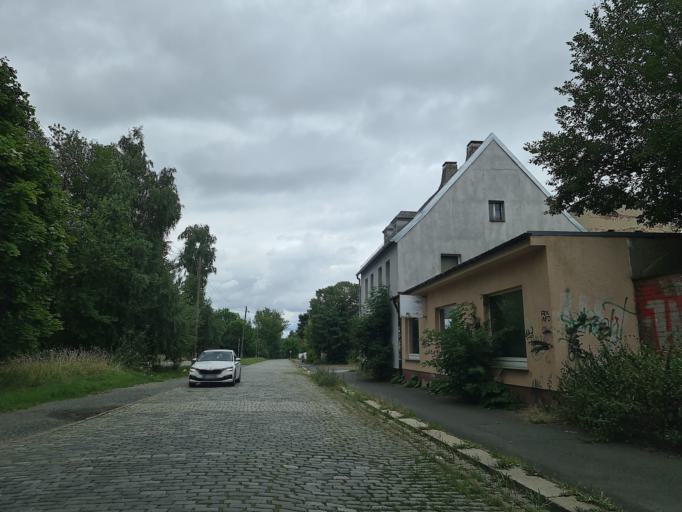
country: DE
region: Saxony
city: Plauen
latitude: 50.5195
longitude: 12.1229
